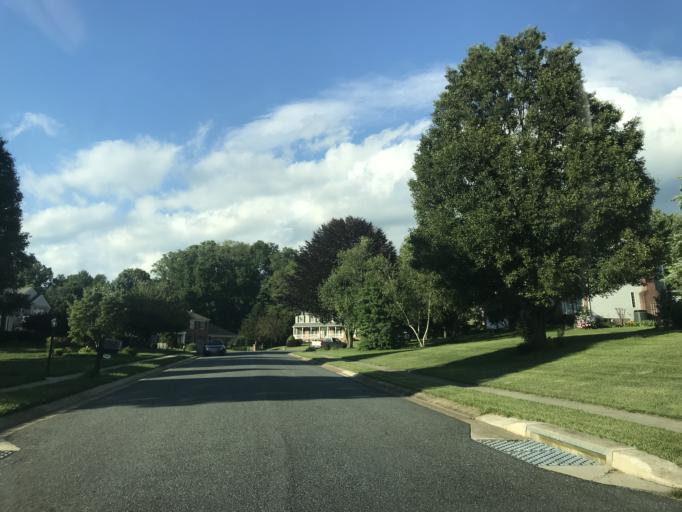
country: US
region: Maryland
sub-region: Harford County
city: South Bel Air
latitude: 39.5635
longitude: -76.3203
